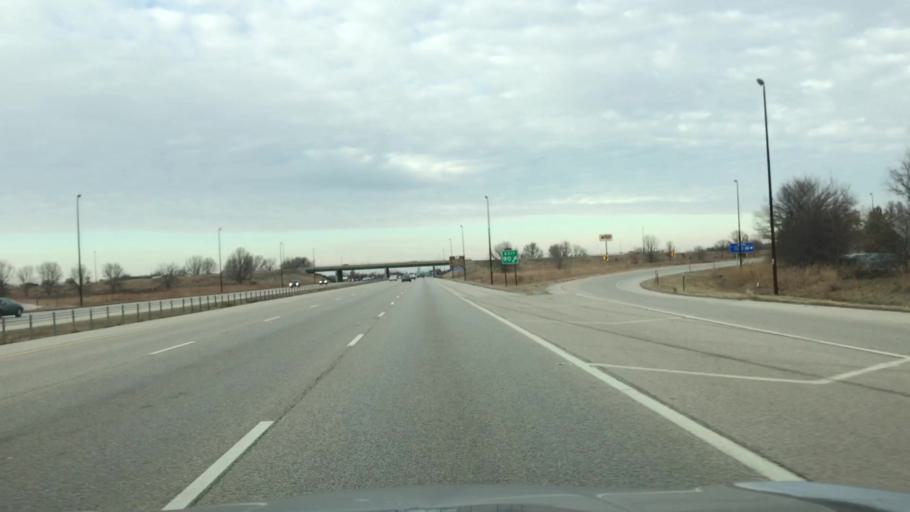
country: US
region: Illinois
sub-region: Sangamon County
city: Southern View
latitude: 39.7105
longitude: -89.6431
